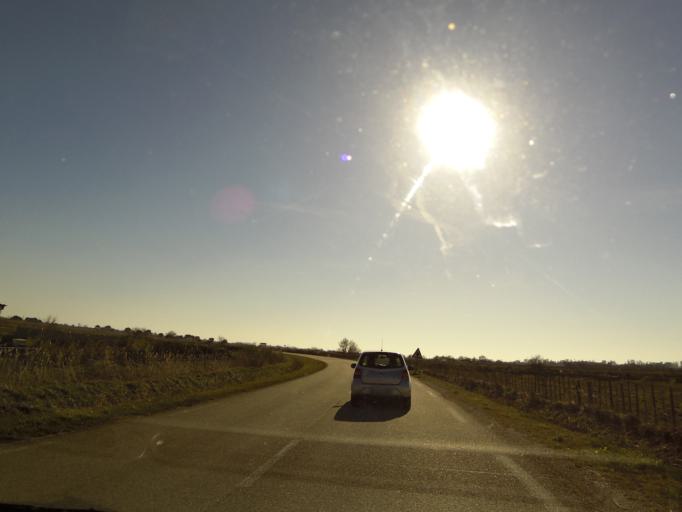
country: FR
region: Provence-Alpes-Cote d'Azur
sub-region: Departement des Bouches-du-Rhone
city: Saintes-Maries-de-la-Mer
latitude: 43.5171
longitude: 4.3729
